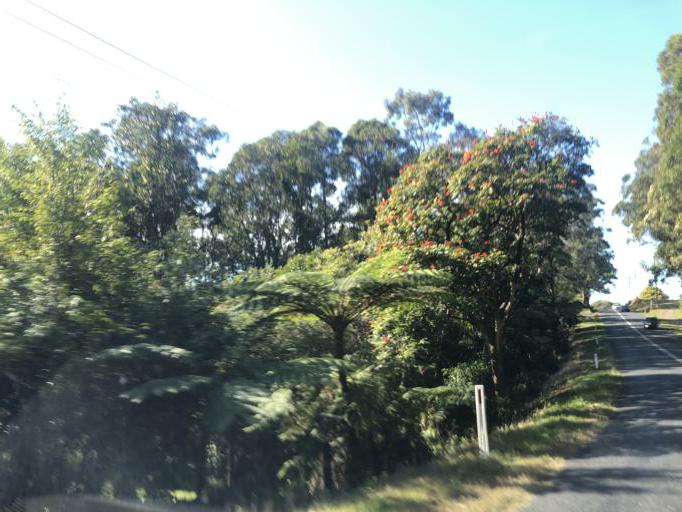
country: AU
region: New South Wales
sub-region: Coffs Harbour
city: Toormina
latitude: -30.3482
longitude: 153.0863
